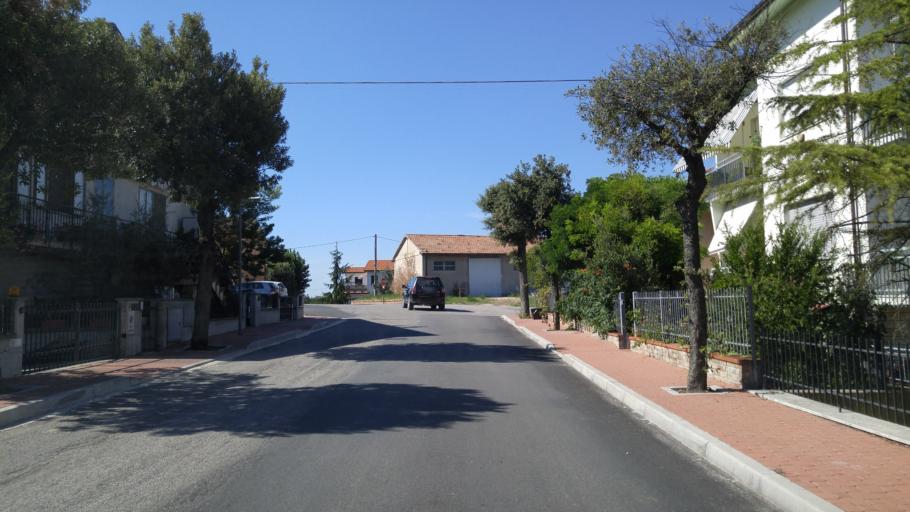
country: IT
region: The Marches
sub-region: Provincia di Pesaro e Urbino
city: San Giorgio di Pesaro
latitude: 43.7175
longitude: 12.9807
